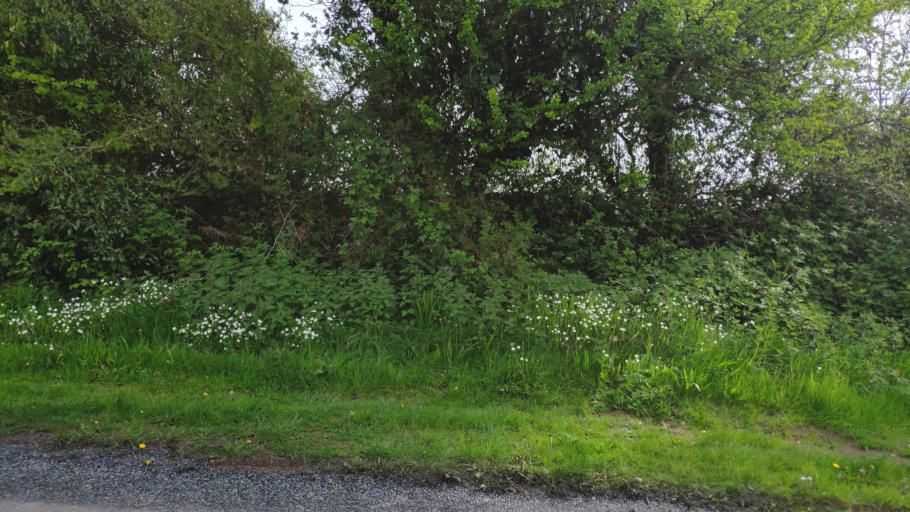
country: IE
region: Munster
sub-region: County Cork
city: Blarney
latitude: 51.9592
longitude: -8.5117
